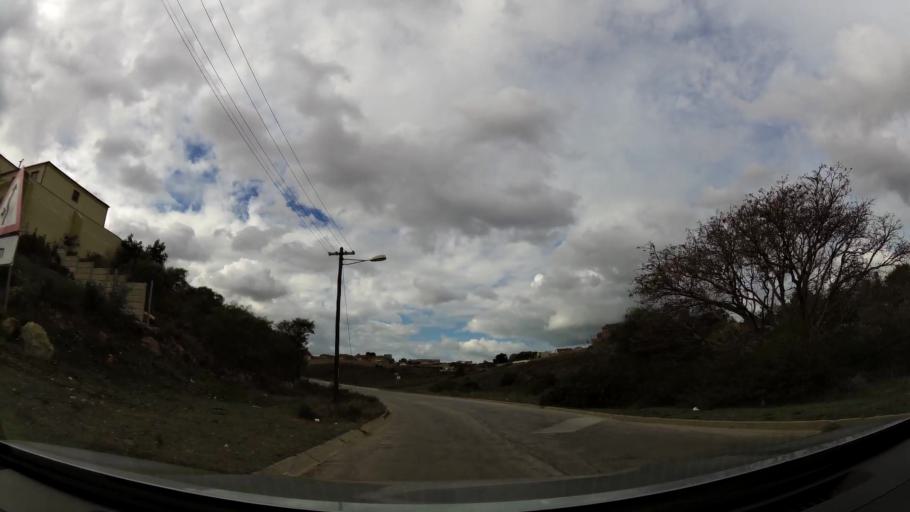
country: ZA
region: Eastern Cape
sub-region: Nelson Mandela Bay Metropolitan Municipality
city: Port Elizabeth
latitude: -33.9356
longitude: 25.5196
